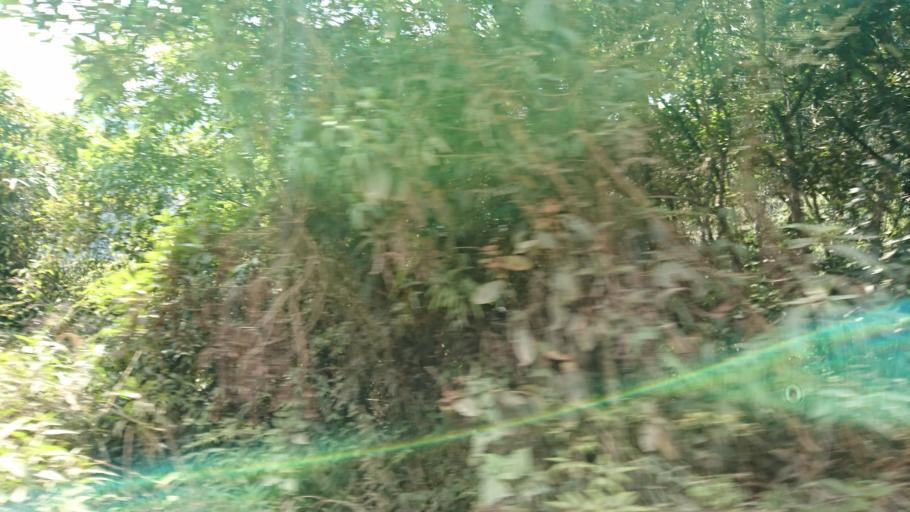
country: BO
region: La Paz
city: Coroico
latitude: -16.1289
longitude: -67.7584
